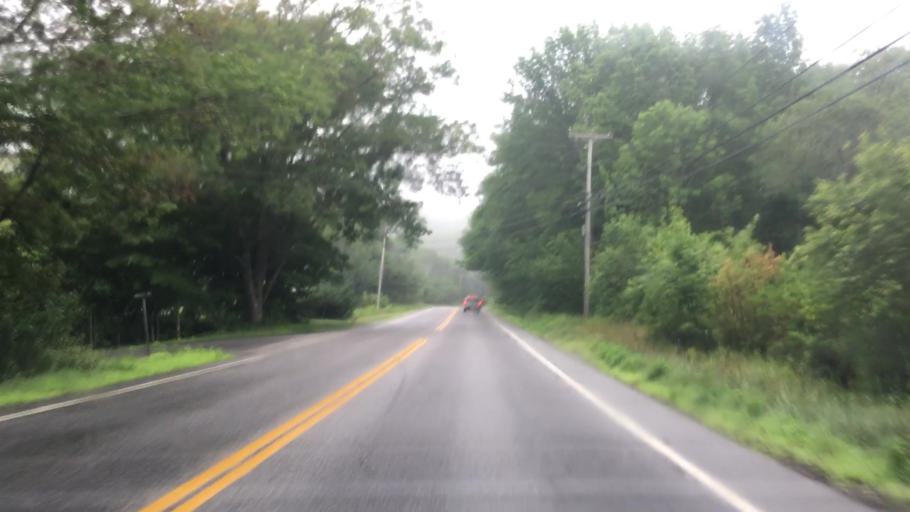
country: US
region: Maine
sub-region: Lincoln County
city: Edgecomb
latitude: 43.9711
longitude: -69.6312
